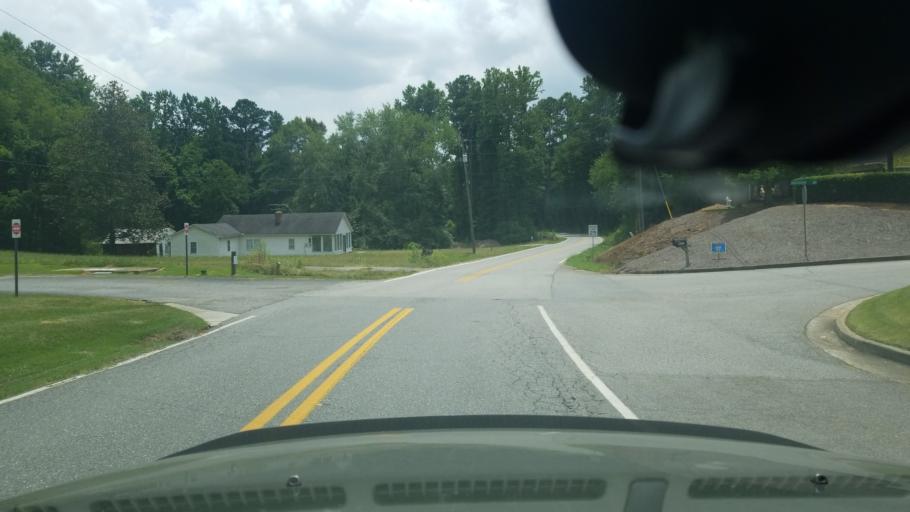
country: US
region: Georgia
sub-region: Fulton County
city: Milton
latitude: 34.1563
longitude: -84.2442
